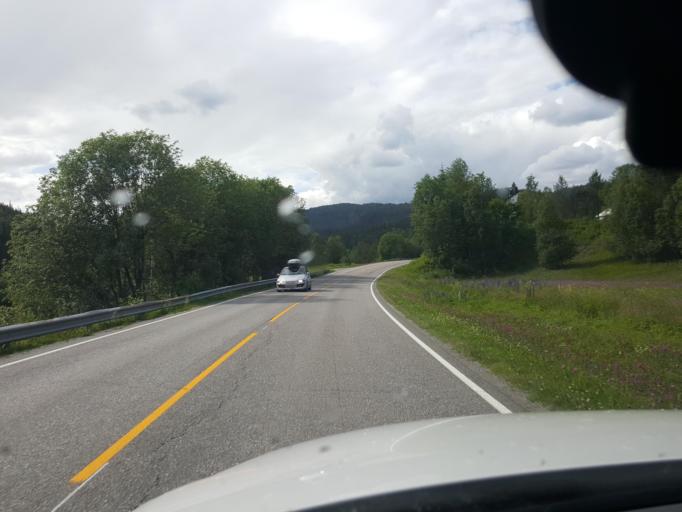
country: NO
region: Nordland
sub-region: Rana
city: Mo i Rana
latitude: 66.4057
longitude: 14.4875
